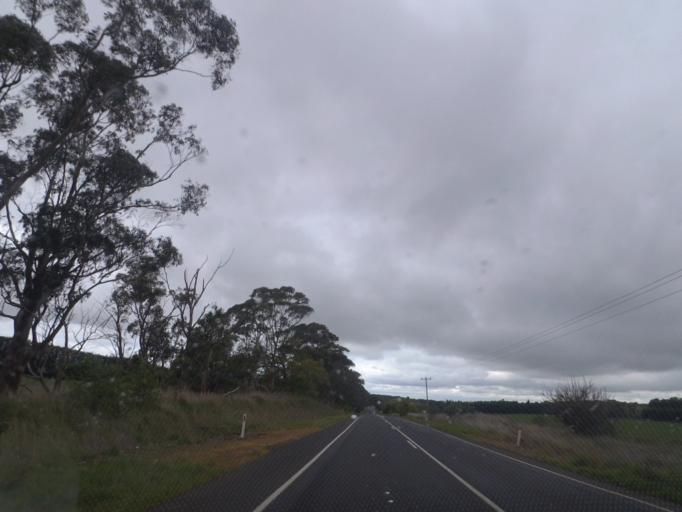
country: AU
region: Victoria
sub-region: Hume
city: Sunbury
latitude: -37.3483
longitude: 144.7083
